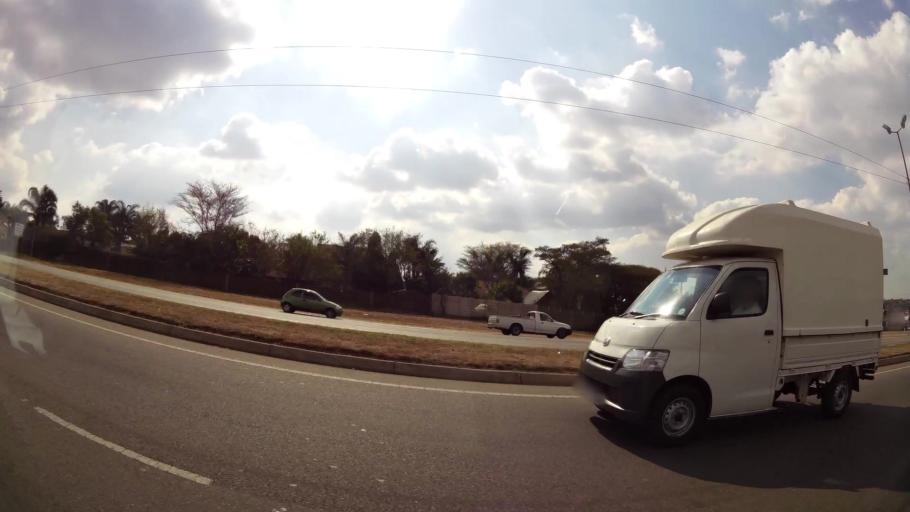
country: ZA
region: Gauteng
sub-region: City of Tshwane Metropolitan Municipality
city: Centurion
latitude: -25.8214
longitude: 28.2597
